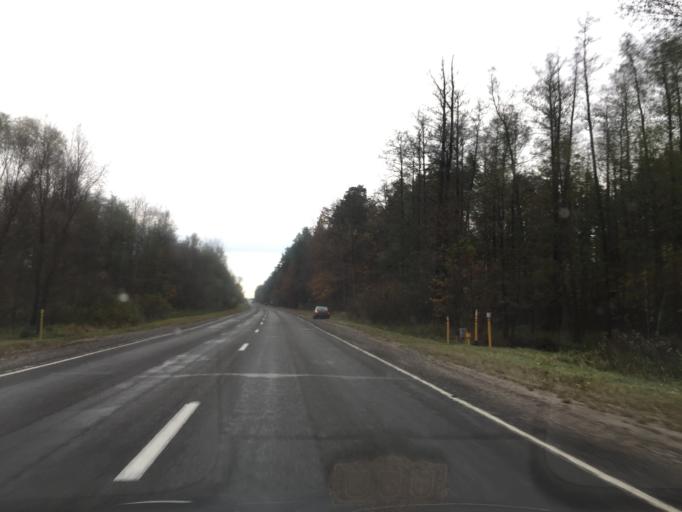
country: BY
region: Gomel
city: Gomel
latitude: 52.4005
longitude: 30.8291
